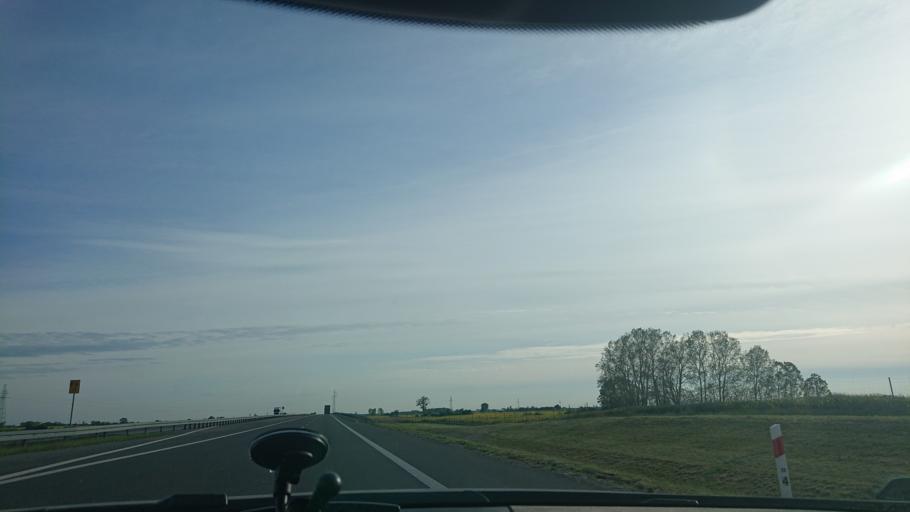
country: PL
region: Greater Poland Voivodeship
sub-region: Powiat gnieznienski
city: Gniezno
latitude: 52.5357
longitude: 17.5204
